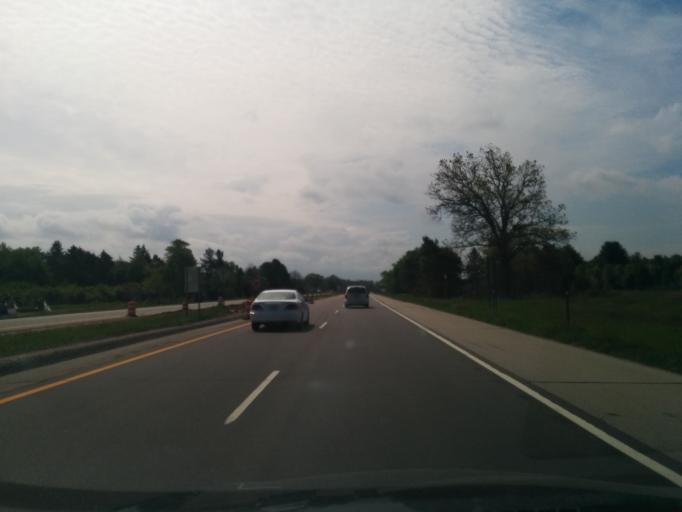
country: US
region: Michigan
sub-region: Ottawa County
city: Beechwood
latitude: 42.9259
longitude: -86.1502
